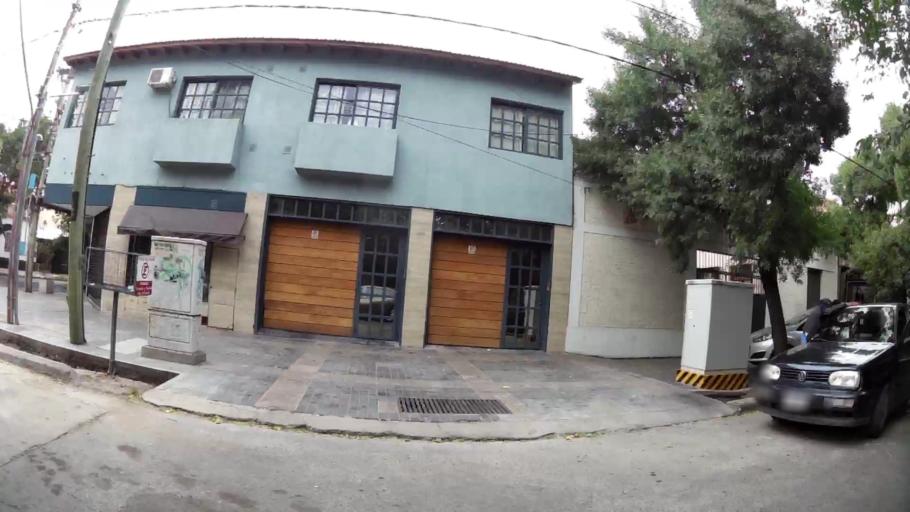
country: AR
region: Mendoza
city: Mendoza
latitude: -32.8860
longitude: -68.8533
